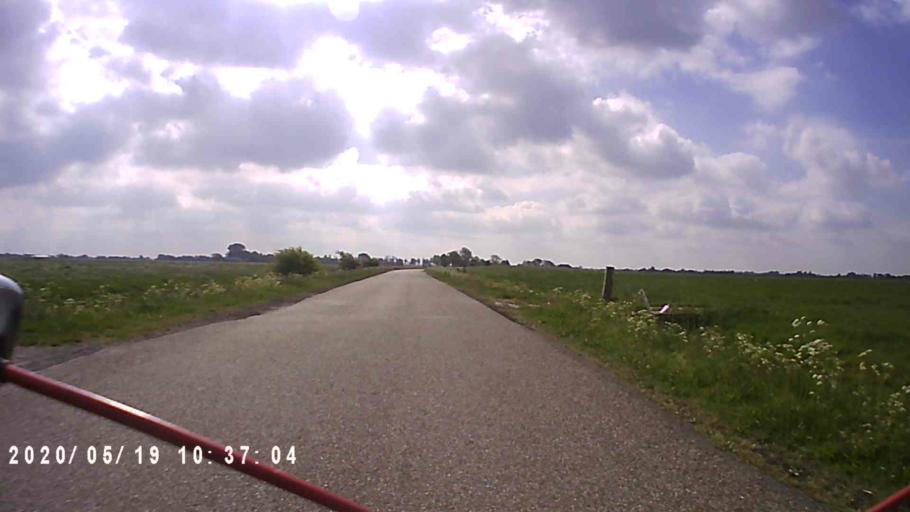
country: NL
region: Friesland
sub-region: Gemeente Kollumerland en Nieuwkruisland
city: Kollum
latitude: 53.2761
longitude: 6.1824
